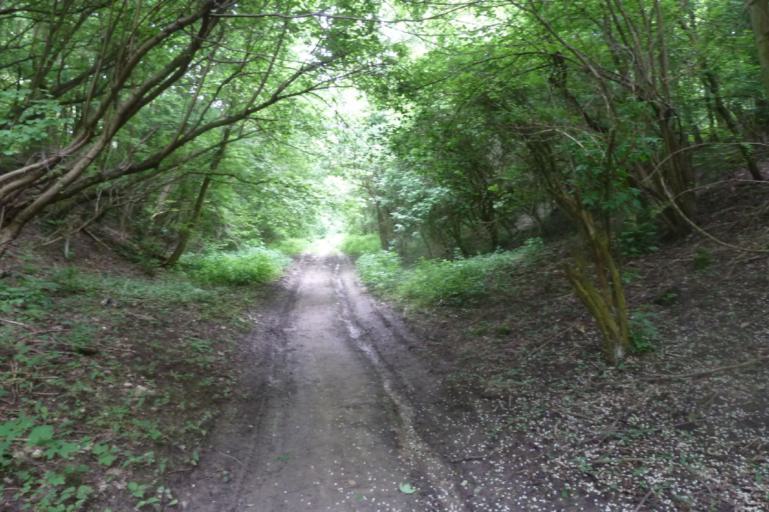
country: HU
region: Komarom-Esztergom
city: Piliscsev
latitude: 47.6880
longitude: 18.8382
